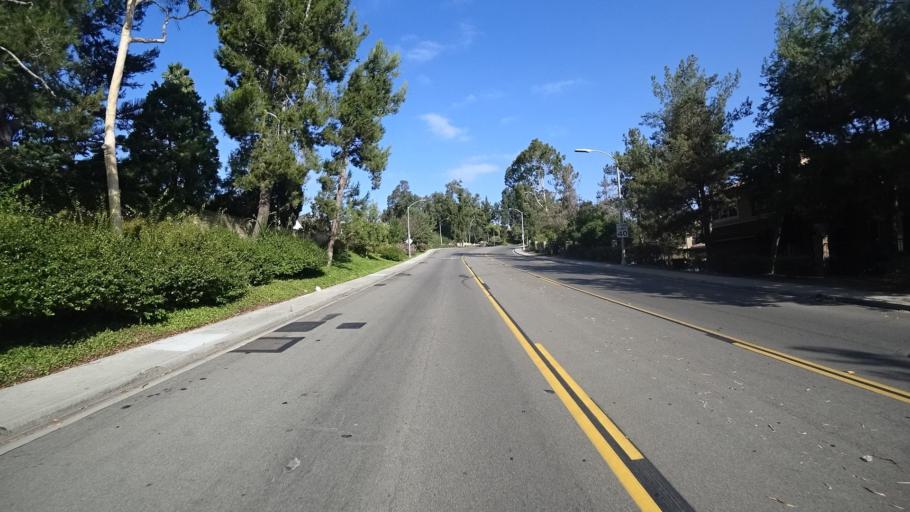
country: US
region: California
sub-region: San Diego County
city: Vista
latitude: 33.1712
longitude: -117.2260
